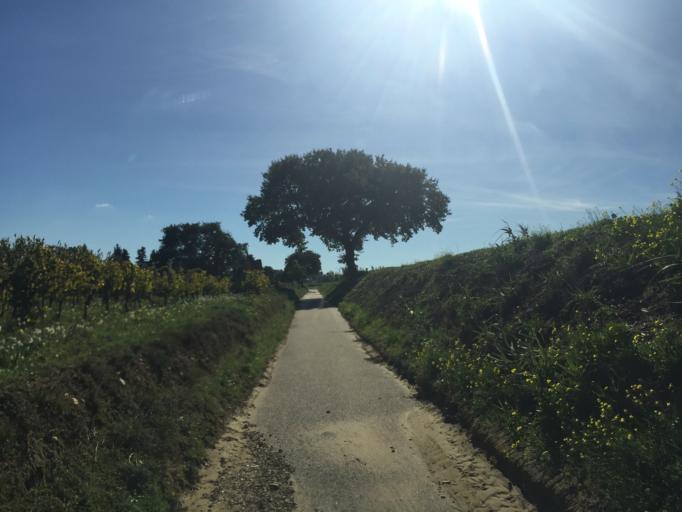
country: FR
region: Provence-Alpes-Cote d'Azur
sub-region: Departement du Vaucluse
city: Courthezon
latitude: 44.0893
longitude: 4.8526
